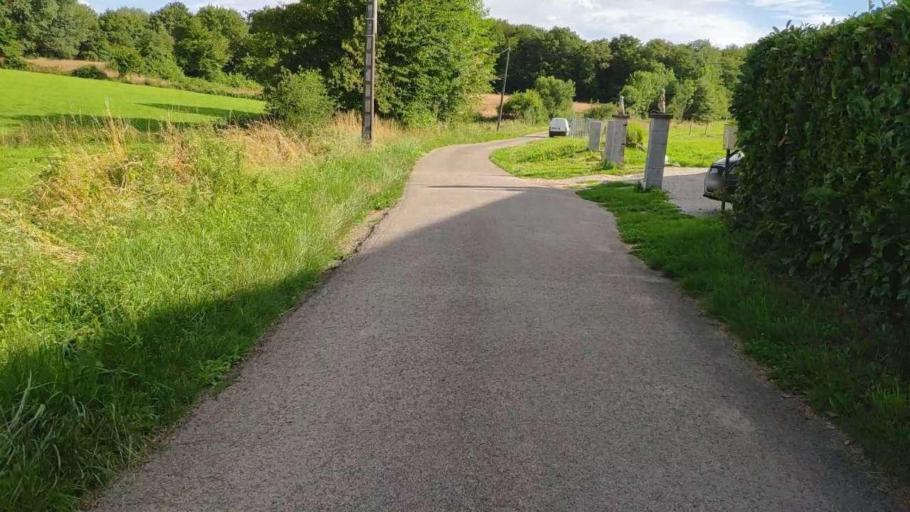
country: FR
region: Franche-Comte
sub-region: Departement du Jura
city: Bletterans
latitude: 46.8047
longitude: 5.5024
